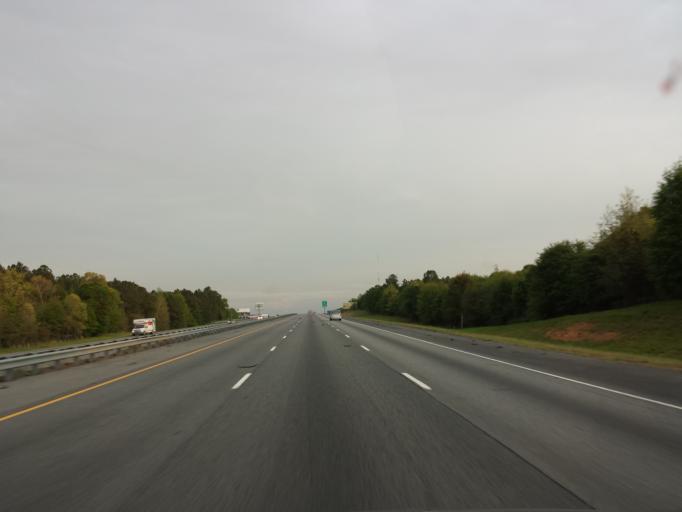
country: US
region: Georgia
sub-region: Crisp County
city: Cordele
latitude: 31.9213
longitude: -83.7437
